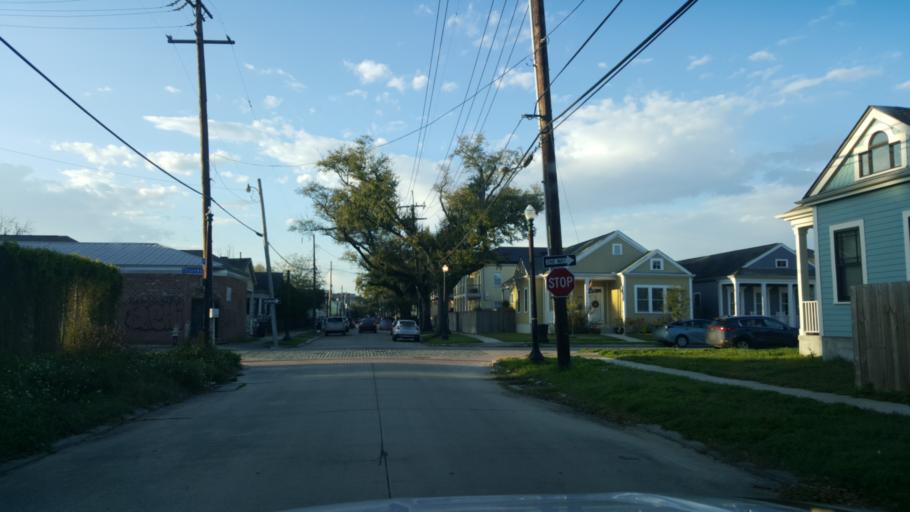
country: US
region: Louisiana
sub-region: Jefferson Parish
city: Gretna
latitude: 29.9268
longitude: -90.0728
